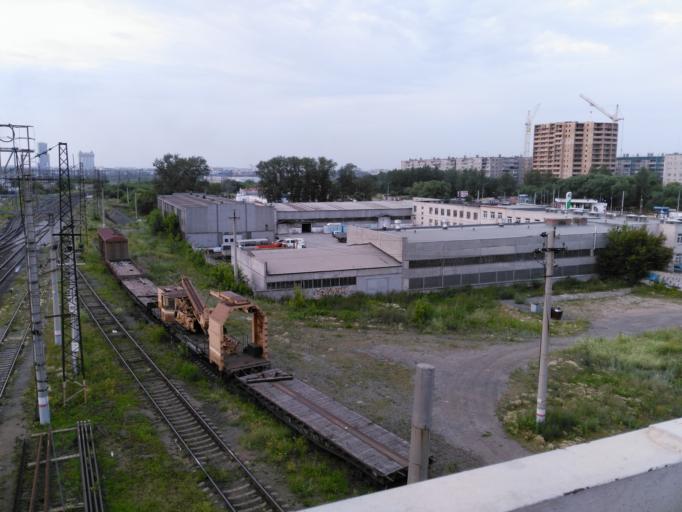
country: RU
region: Chelyabinsk
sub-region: Gorod Chelyabinsk
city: Chelyabinsk
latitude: 55.1460
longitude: 61.4231
